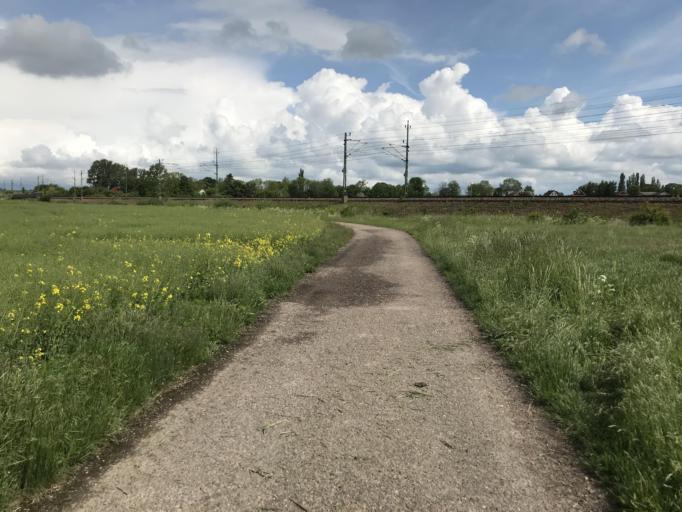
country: SE
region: Skane
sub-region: Landskrona
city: Landskrona
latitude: 55.9007
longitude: 12.8493
